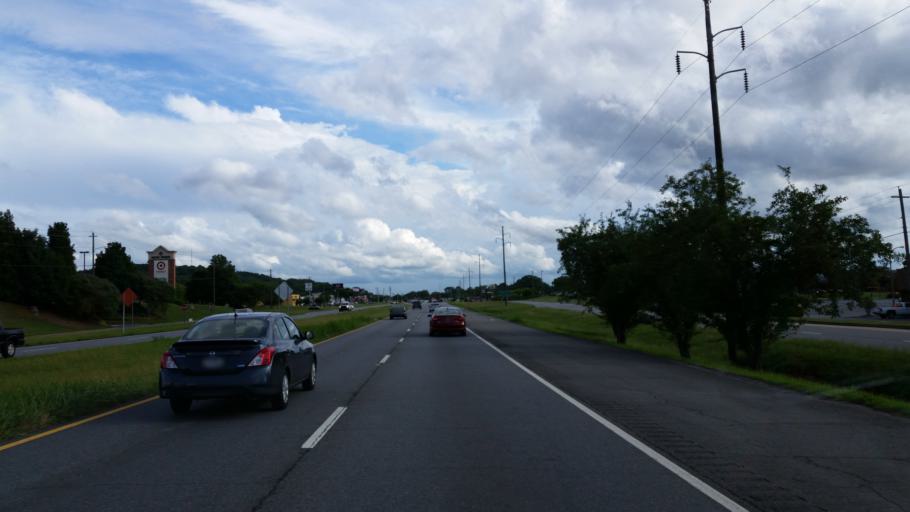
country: US
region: Georgia
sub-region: Bartow County
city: Cartersville
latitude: 34.1739
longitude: -84.7869
